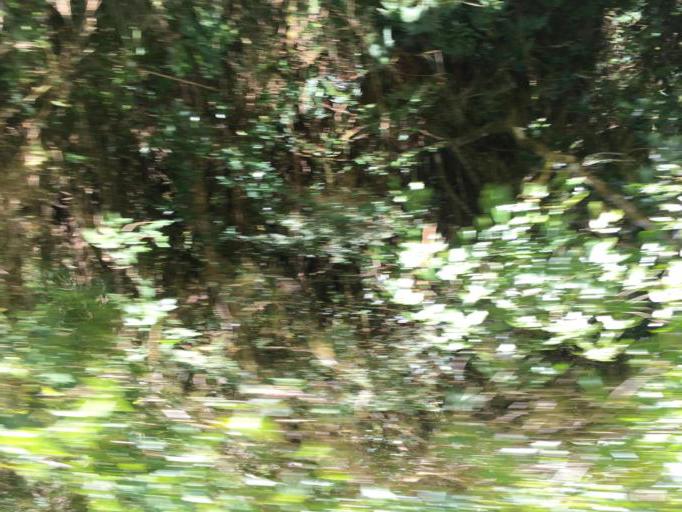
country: TW
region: Taiwan
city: Daxi
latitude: 24.5580
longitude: 121.3977
